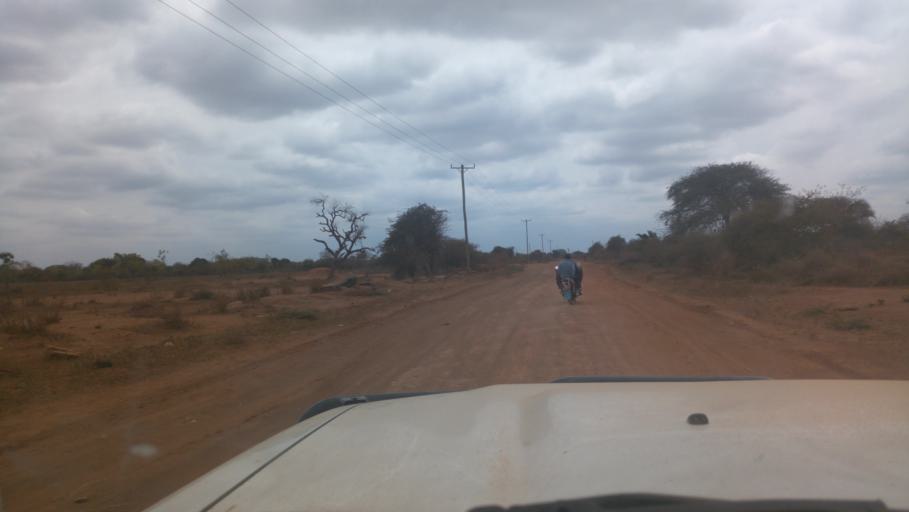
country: KE
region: Makueni
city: Wote
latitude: -1.7966
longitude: 37.9235
